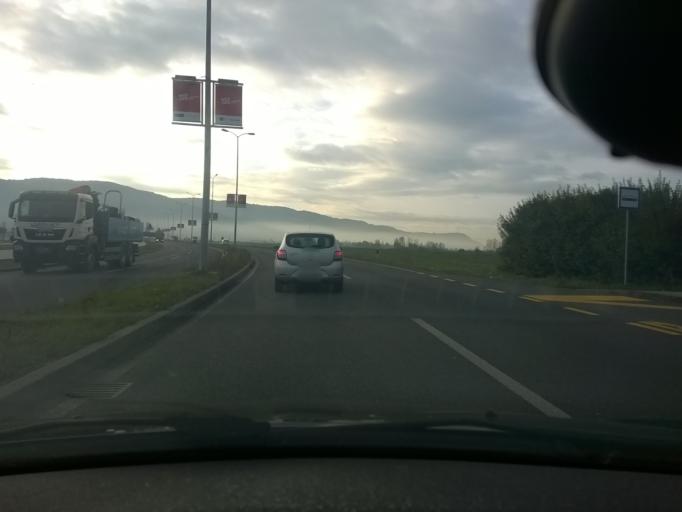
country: HR
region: Zagrebacka
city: Zapresic
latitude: 45.8717
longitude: 15.8215
